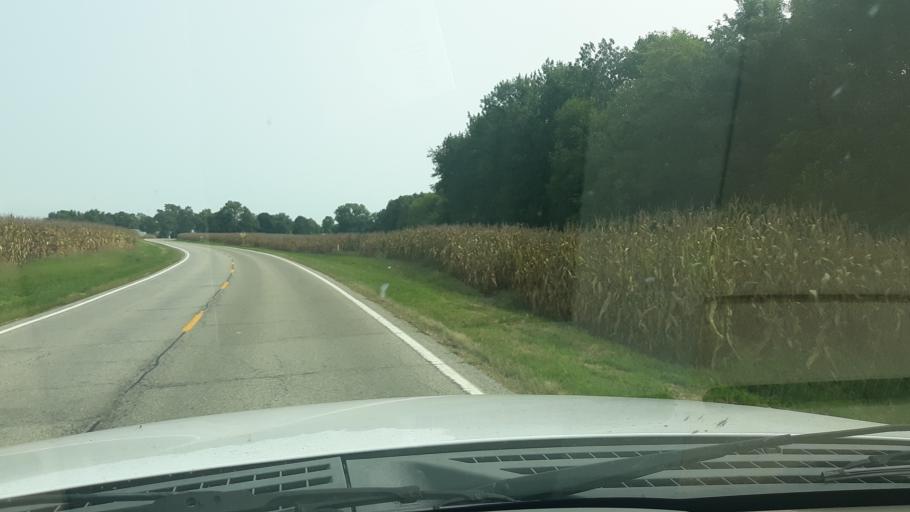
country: US
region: Illinois
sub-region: Edwards County
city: Grayville
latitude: 38.3065
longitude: -87.9441
